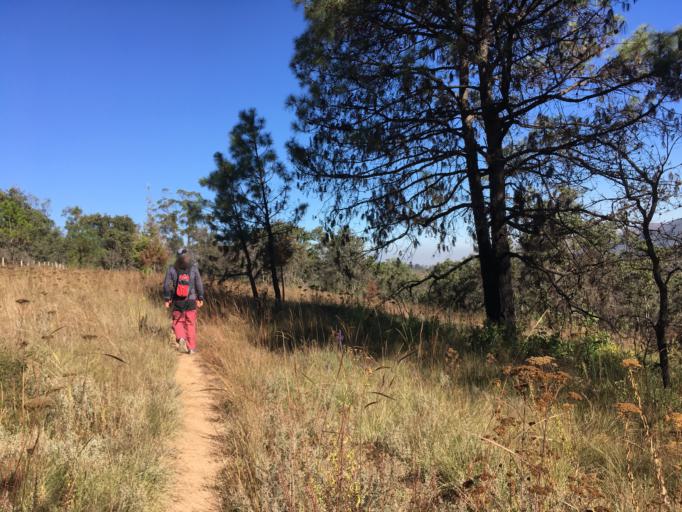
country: MX
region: Michoacan
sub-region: Morelia
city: Montana Monarca (Punta Altozano)
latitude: 19.6649
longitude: -101.1450
